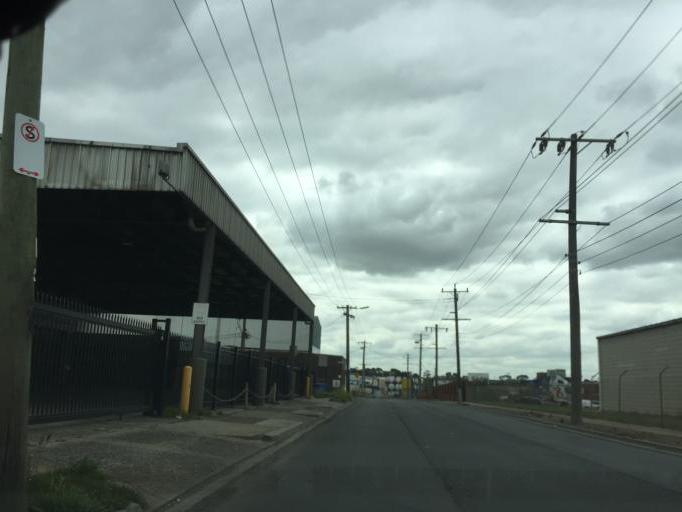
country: AU
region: Victoria
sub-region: Brimbank
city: Brooklyn
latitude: -37.8076
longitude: 144.8517
